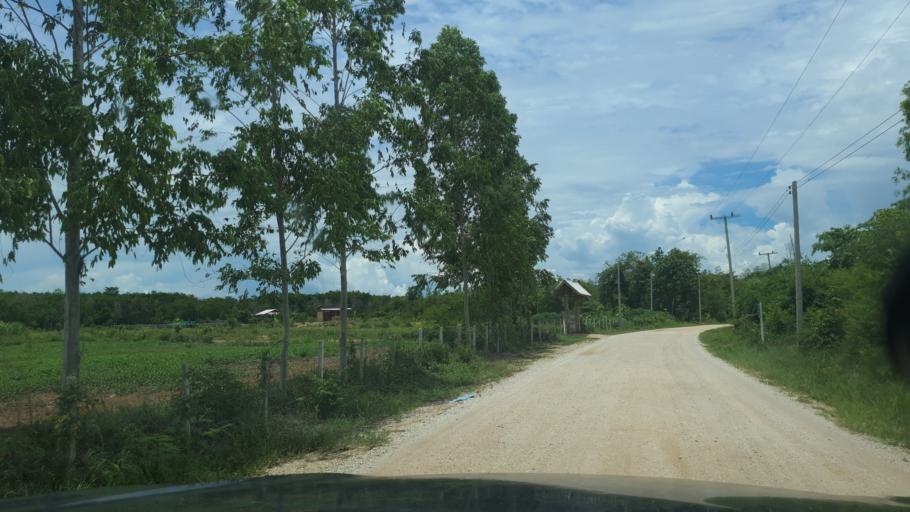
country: TH
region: Lampang
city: Ko Kha
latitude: 18.1887
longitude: 99.3201
